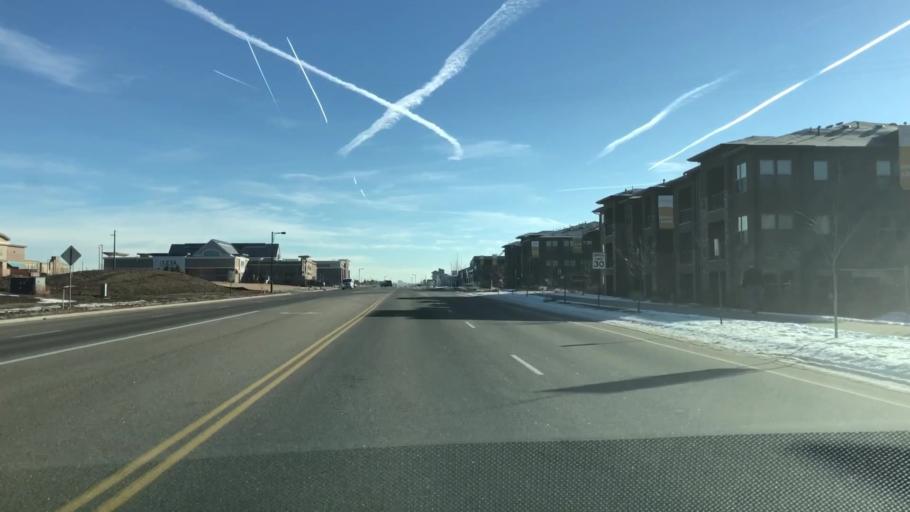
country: US
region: Colorado
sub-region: Larimer County
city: Loveland
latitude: 40.4034
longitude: -104.9859
